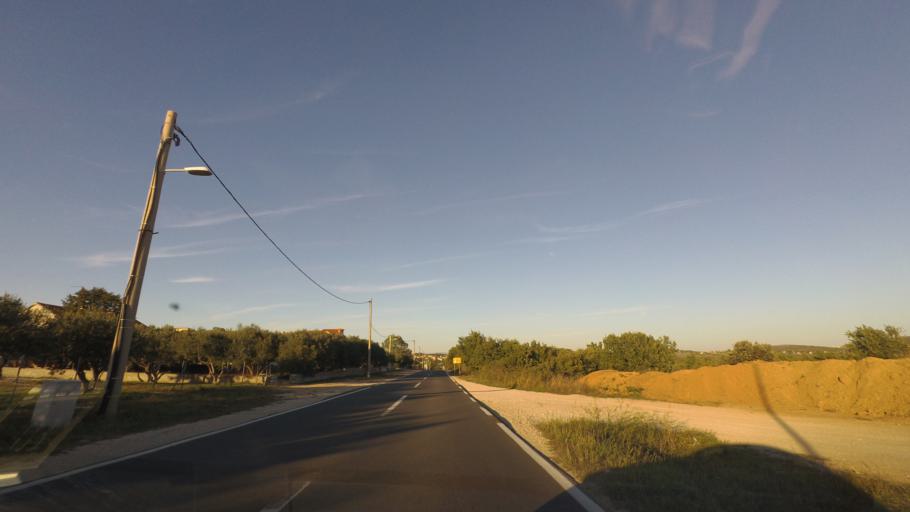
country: HR
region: Zadarska
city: Polaca
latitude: 44.0055
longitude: 15.5050
